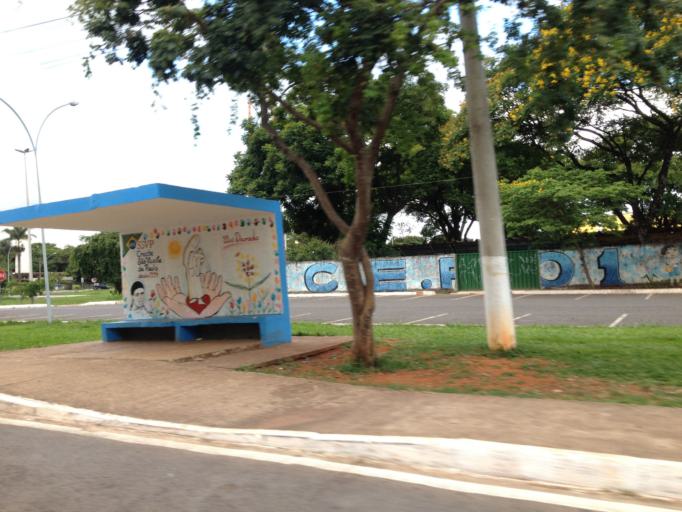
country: BR
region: Federal District
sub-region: Brasilia
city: Brasilia
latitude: -15.7846
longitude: -47.9372
